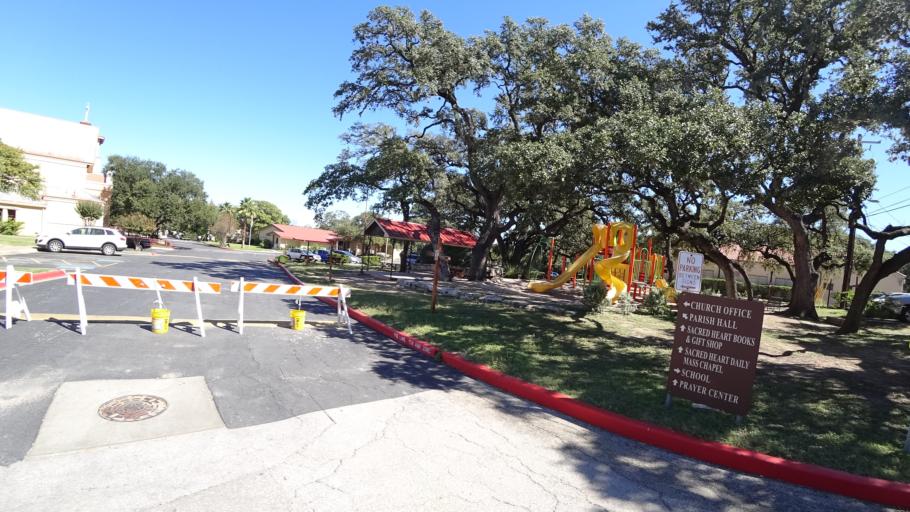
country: US
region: Texas
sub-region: Travis County
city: Austin
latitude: 30.2414
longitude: -97.7633
